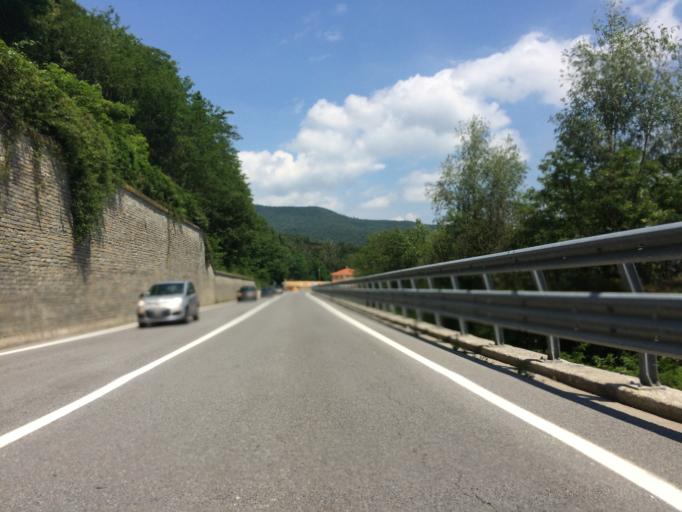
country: IT
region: Piedmont
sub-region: Provincia di Cuneo
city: Priola
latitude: 44.2533
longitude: 8.0204
